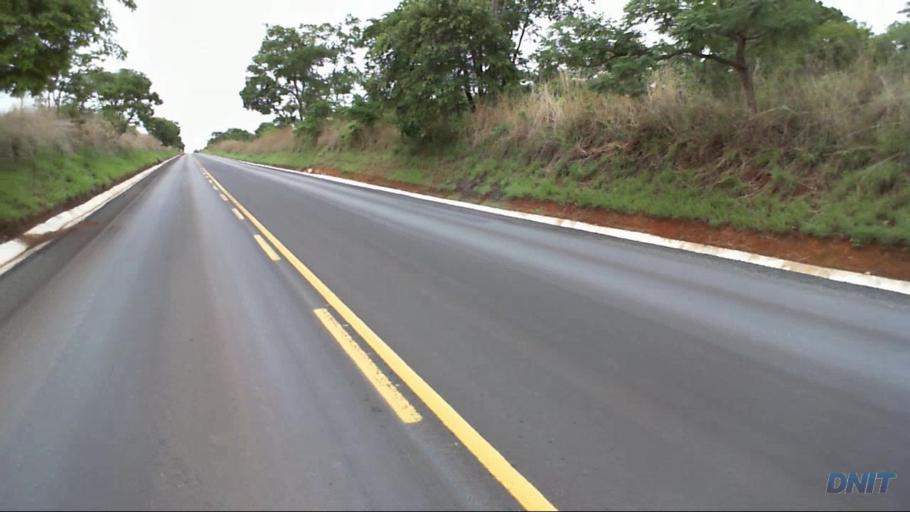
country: BR
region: Goias
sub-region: Padre Bernardo
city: Padre Bernardo
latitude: -15.1780
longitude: -48.4163
